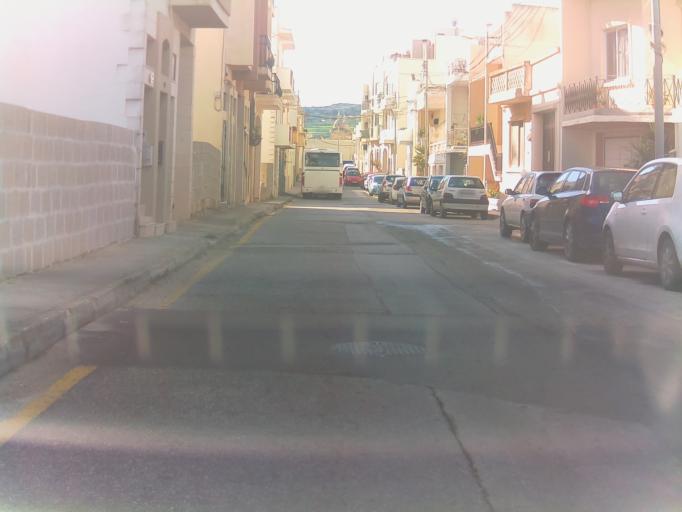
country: MT
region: L-Imgarr
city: Imgarr
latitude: 35.9234
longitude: 14.3671
